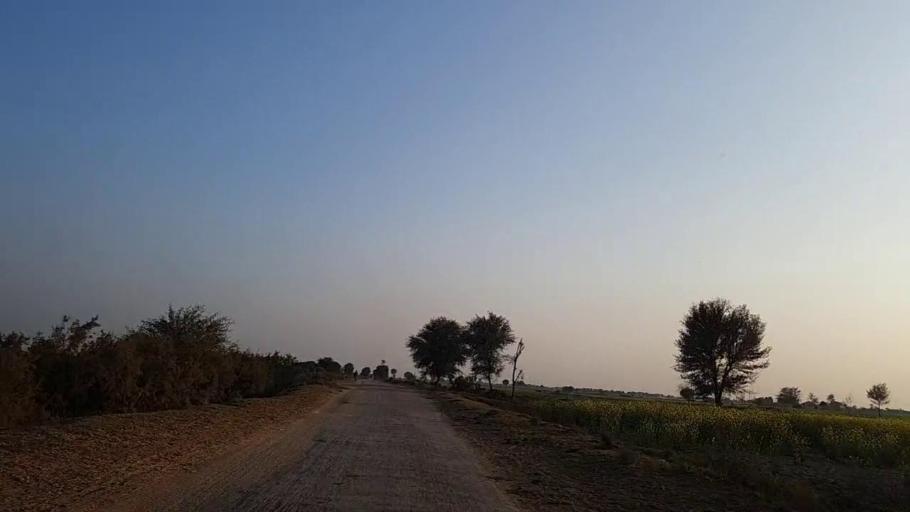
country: PK
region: Sindh
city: Shahdadpur
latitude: 26.0119
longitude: 68.4907
